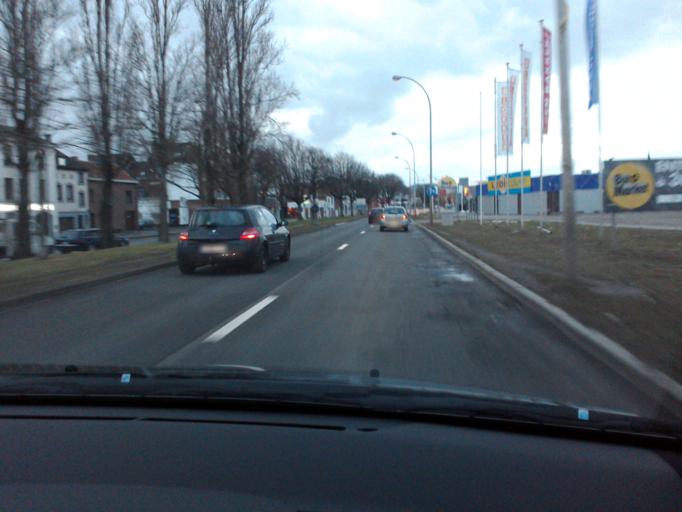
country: BE
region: Wallonia
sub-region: Province de Liege
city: Liege
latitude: 50.6239
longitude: 5.5912
